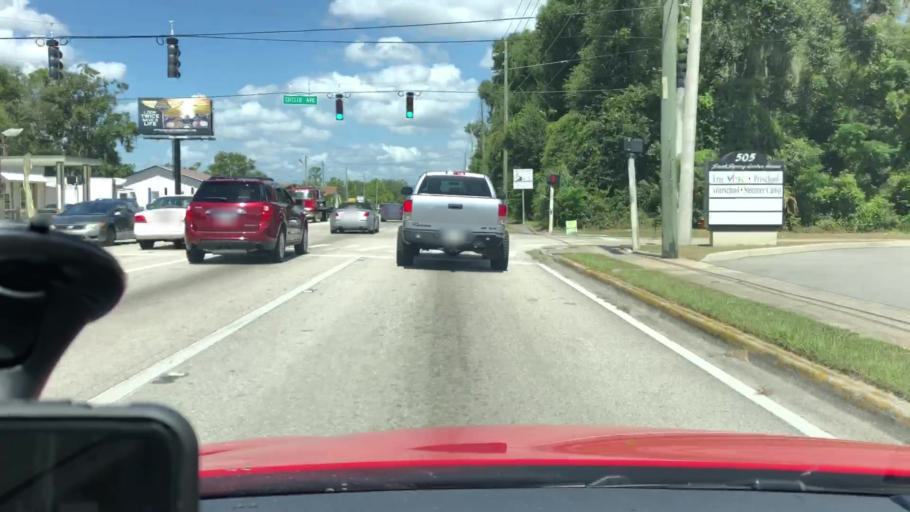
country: US
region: Florida
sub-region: Volusia County
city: West DeLand
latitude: 29.0205
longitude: -81.3239
